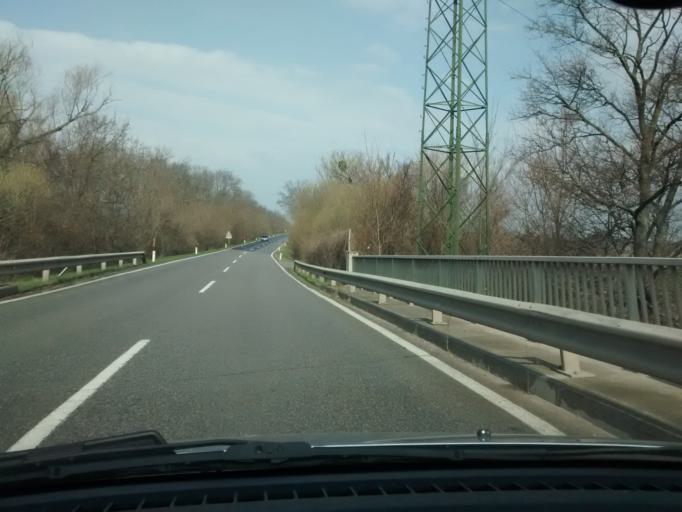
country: AT
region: Lower Austria
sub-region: Politischer Bezirk Modling
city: Munchendorf
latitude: 48.0428
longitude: 16.3726
